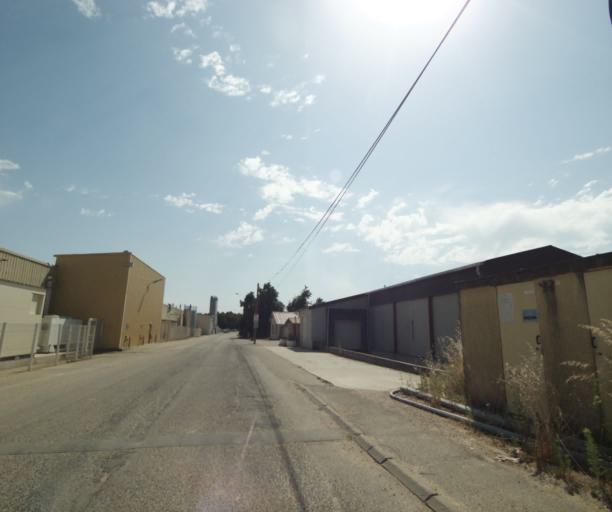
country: FR
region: Midi-Pyrenees
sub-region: Departement du Tarn-et-Garonne
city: Bressols
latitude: 43.9835
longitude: 1.3245
